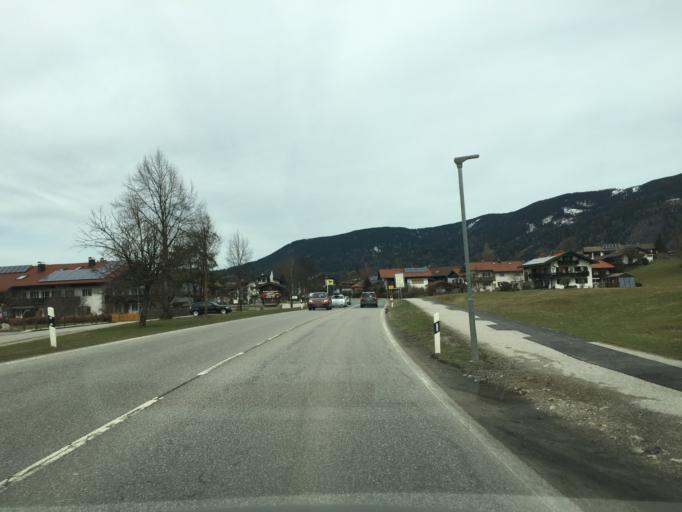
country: DE
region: Bavaria
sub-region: Upper Bavaria
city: Inzell
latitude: 47.7580
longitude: 12.7500
